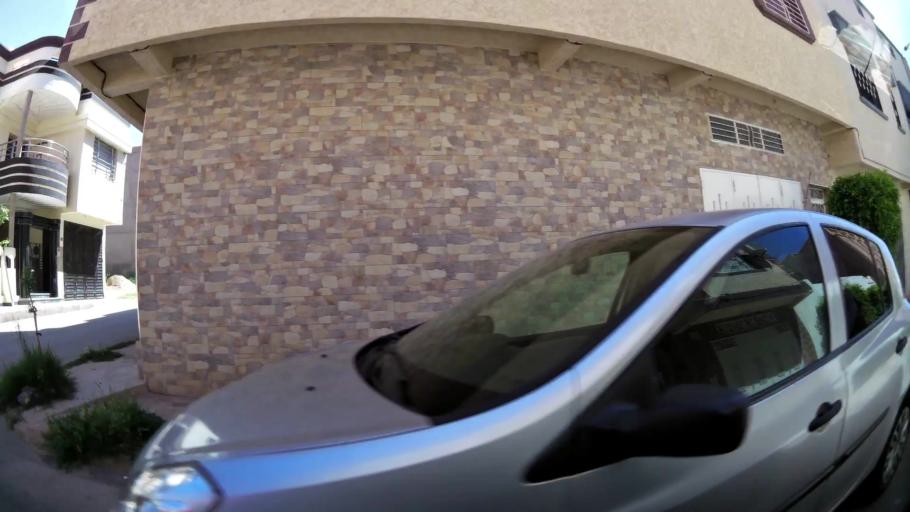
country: MA
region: Oriental
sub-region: Oujda-Angad
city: Oujda
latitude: 34.6495
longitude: -1.9115
